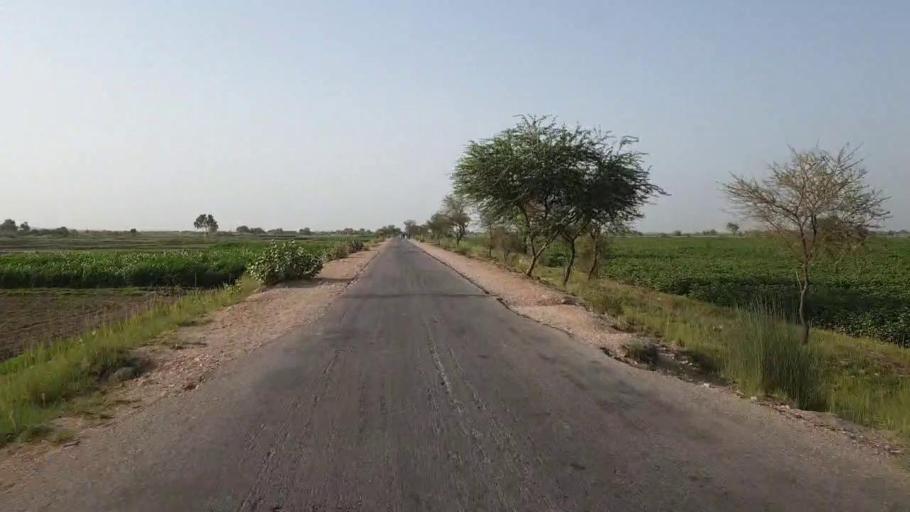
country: PK
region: Sindh
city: Jam Sahib
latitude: 26.4637
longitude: 68.8588
